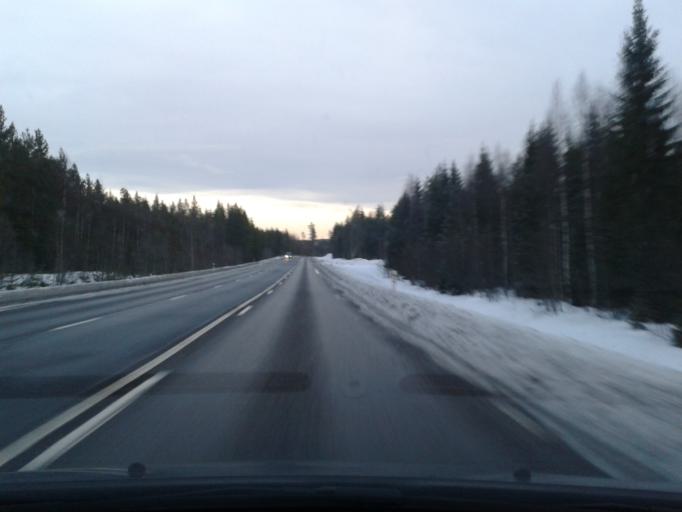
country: SE
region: Vaesternorrland
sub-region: Kramfors Kommun
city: Bollstabruk
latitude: 63.1081
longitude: 17.5052
